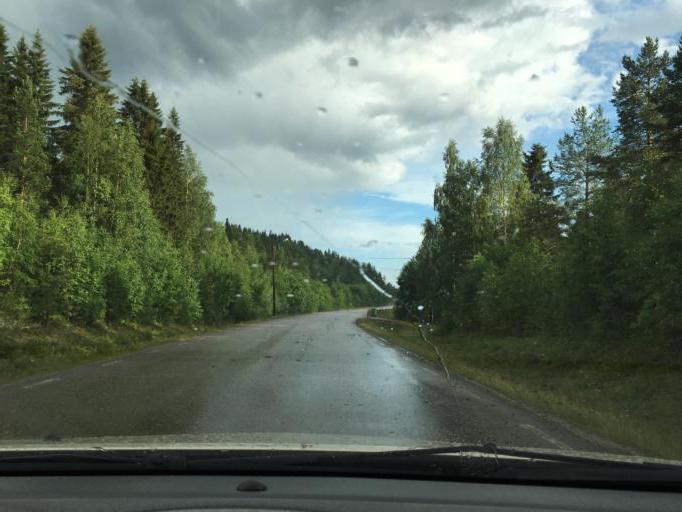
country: SE
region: Norrbotten
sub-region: Kalix Kommun
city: Rolfs
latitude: 65.9367
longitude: 22.8922
